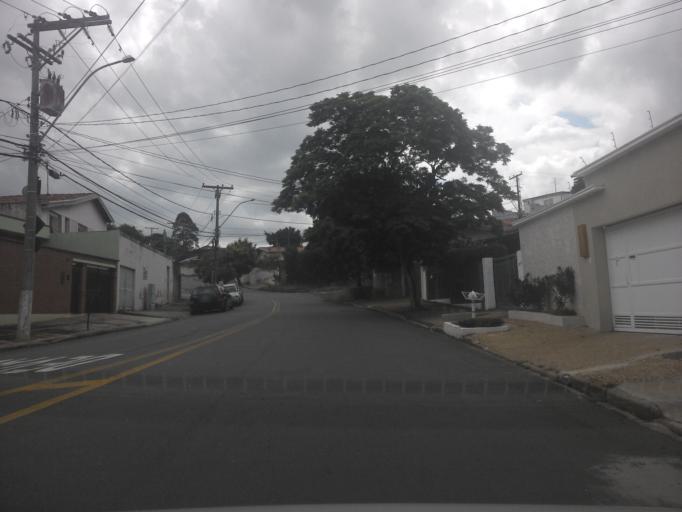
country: BR
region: Sao Paulo
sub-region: Campinas
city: Campinas
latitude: -22.8693
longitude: -47.0382
